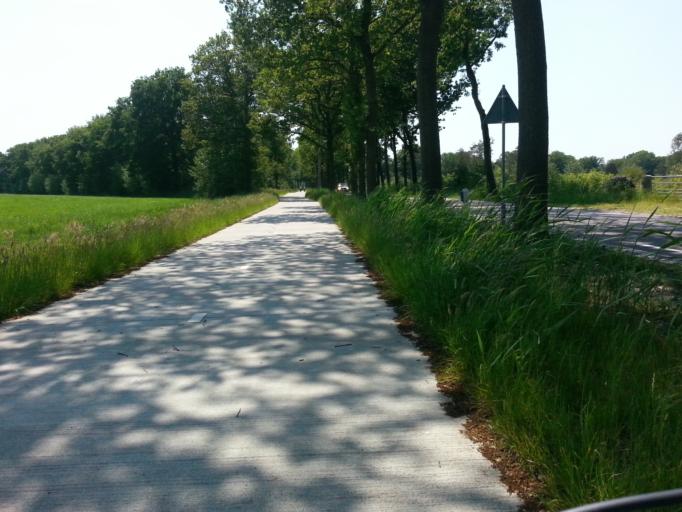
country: NL
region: Utrecht
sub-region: Gemeente Leusden
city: Leusden
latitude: 52.1279
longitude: 5.4811
